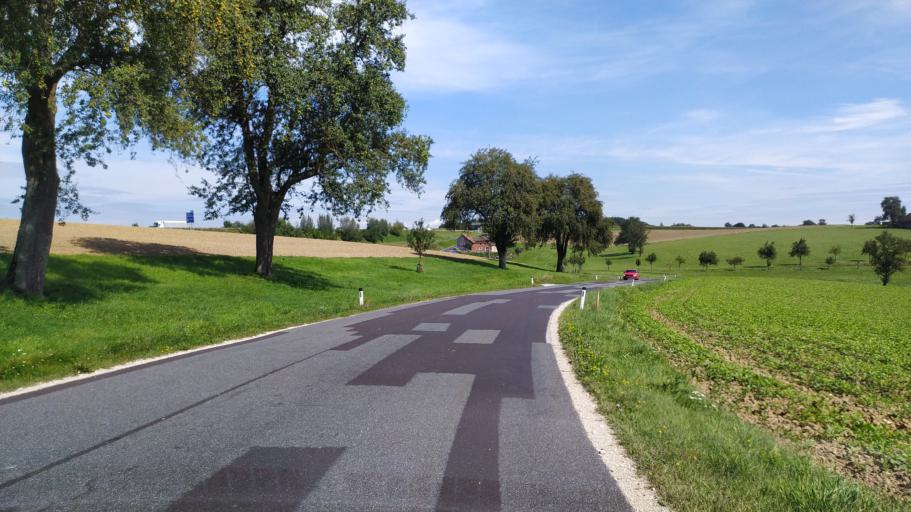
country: AT
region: Lower Austria
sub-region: Politischer Bezirk Amstetten
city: Wolfsbach
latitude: 48.1139
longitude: 14.7092
